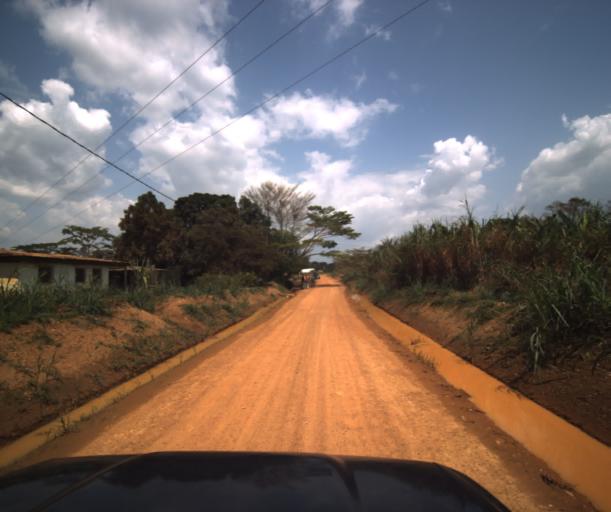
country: CM
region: Centre
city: Akono
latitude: 3.5500
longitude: 11.0547
